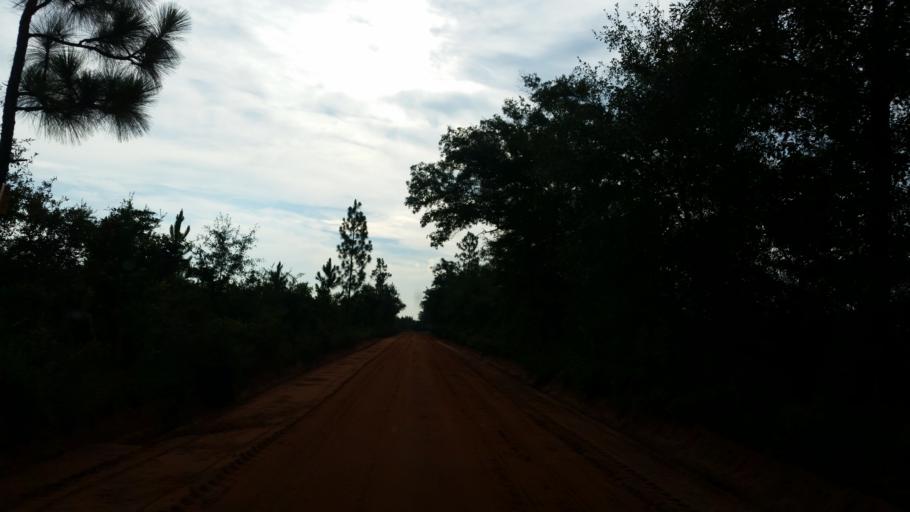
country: US
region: Alabama
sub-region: Escambia County
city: Atmore
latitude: 30.7934
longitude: -87.5465
